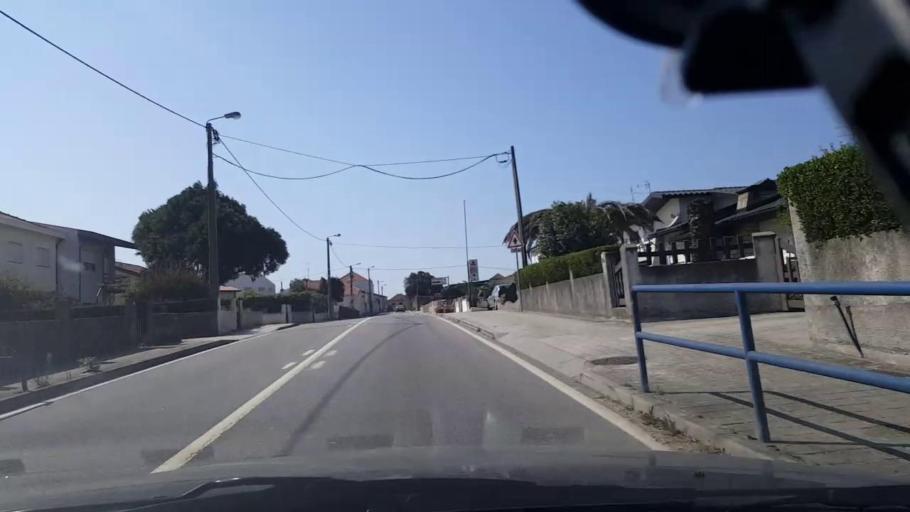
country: PT
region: Porto
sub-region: Povoa de Varzim
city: Pedroso
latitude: 41.3898
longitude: -8.7040
